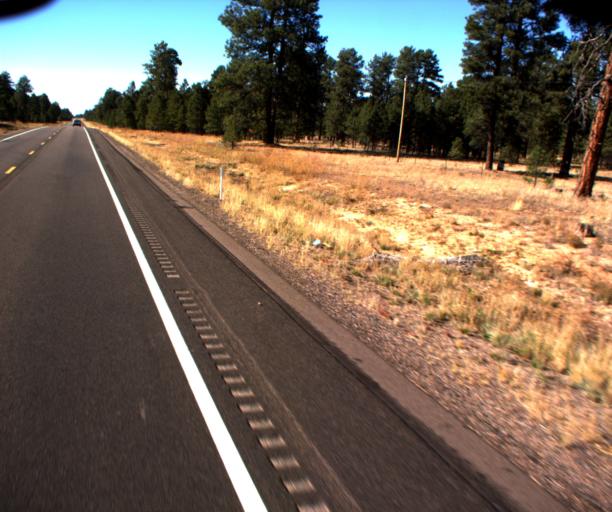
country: US
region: Arizona
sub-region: Apache County
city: Saint Michaels
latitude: 35.6883
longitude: -109.2483
